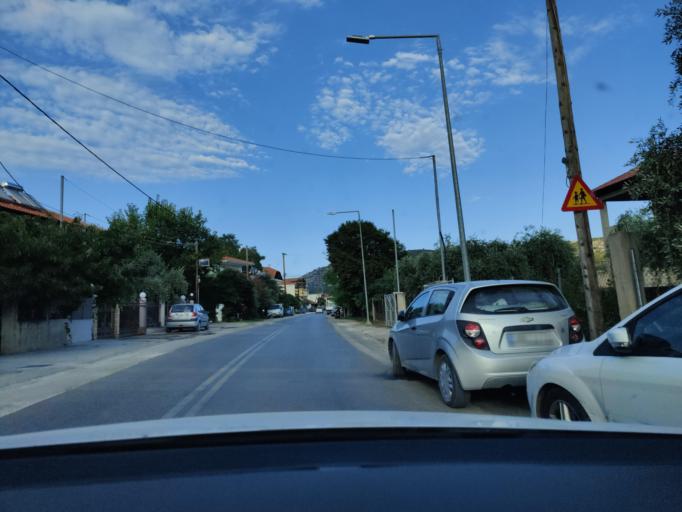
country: GR
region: East Macedonia and Thrace
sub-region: Nomos Kavalas
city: Limenaria
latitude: 40.6116
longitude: 24.6134
